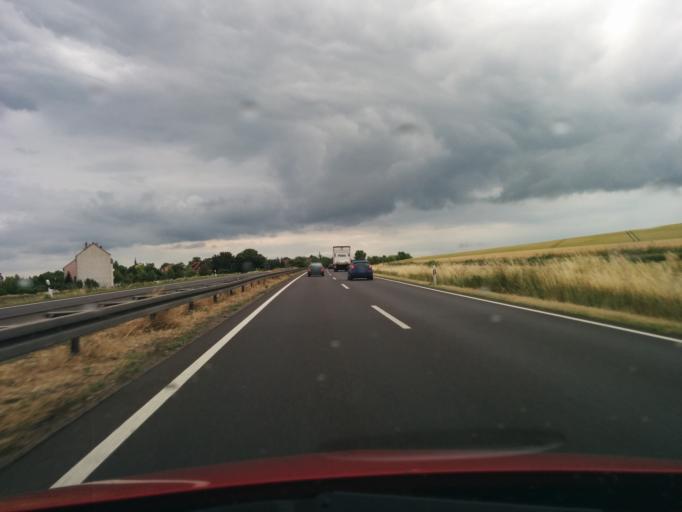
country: DE
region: Thuringia
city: Walschleben
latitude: 51.0707
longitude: 10.9258
